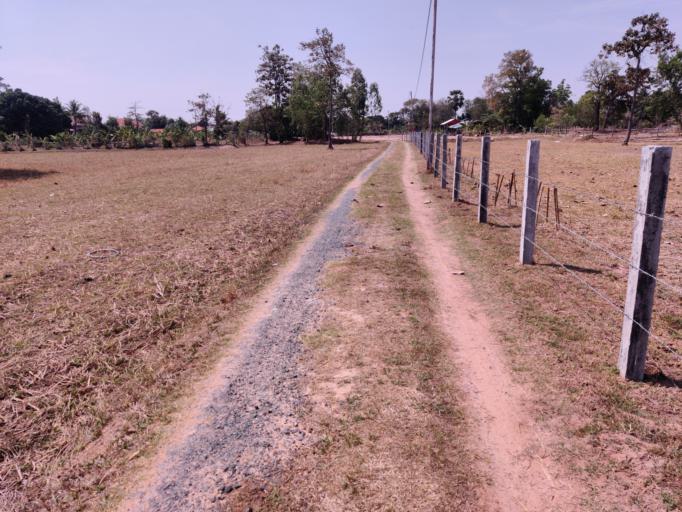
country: TH
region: Sisaket
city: Huai Thap Than
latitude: 15.0527
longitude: 104.0413
